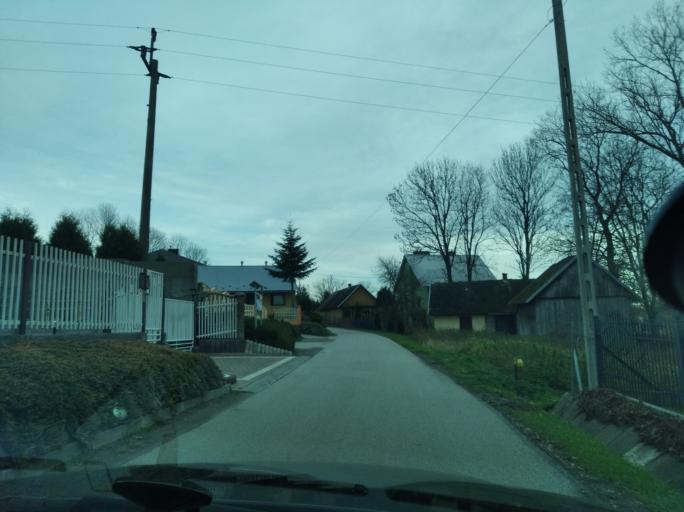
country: PL
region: Subcarpathian Voivodeship
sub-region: Powiat przeworski
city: Debow
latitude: 50.0480
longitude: 22.4370
